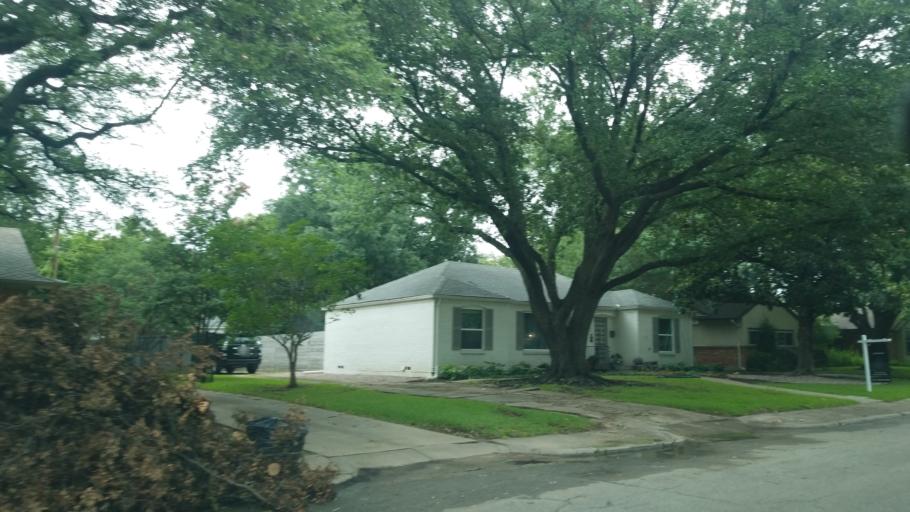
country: US
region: Texas
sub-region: Dallas County
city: Farmers Branch
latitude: 32.8924
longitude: -96.8592
